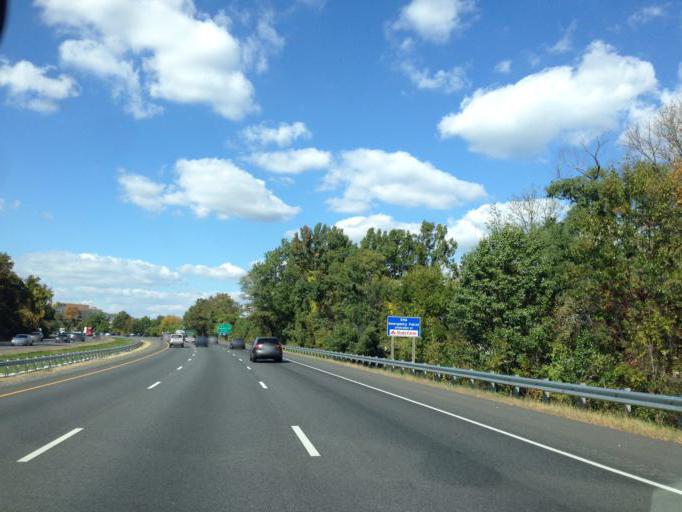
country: US
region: Maryland
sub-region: Baltimore County
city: Timonium
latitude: 39.4455
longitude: -76.6353
